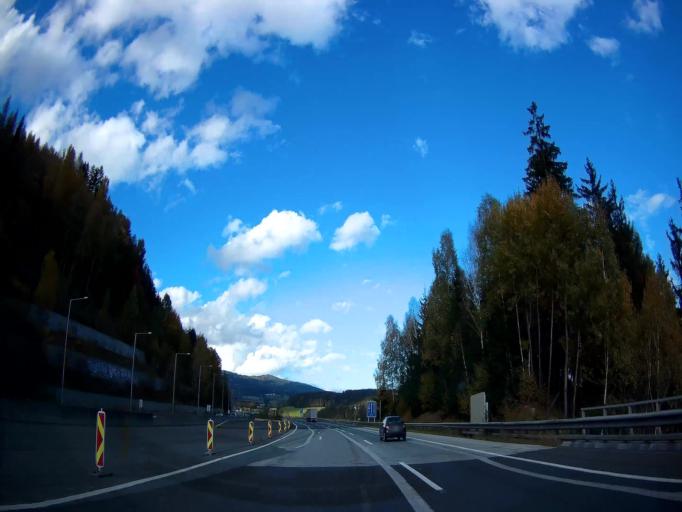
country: AT
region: Carinthia
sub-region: Politischer Bezirk Wolfsberg
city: Bad Sankt Leonhard im Lavanttal
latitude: 46.9152
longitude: 14.8376
